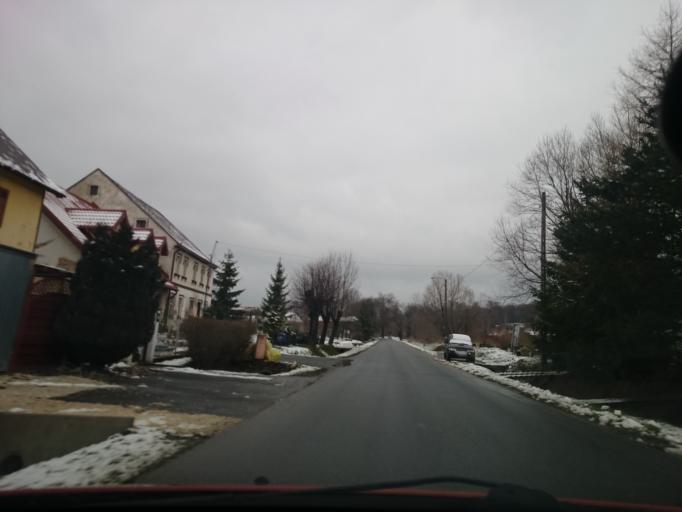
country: PL
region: Lower Silesian Voivodeship
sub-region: Powiat klodzki
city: Klodzko
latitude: 50.3832
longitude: 16.6625
